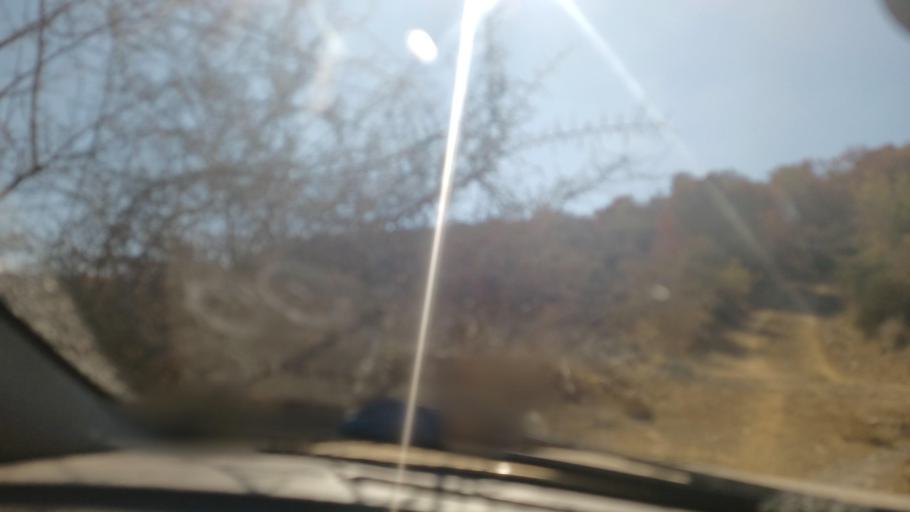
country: CY
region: Pafos
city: Polis
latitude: 34.9447
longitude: 32.4854
